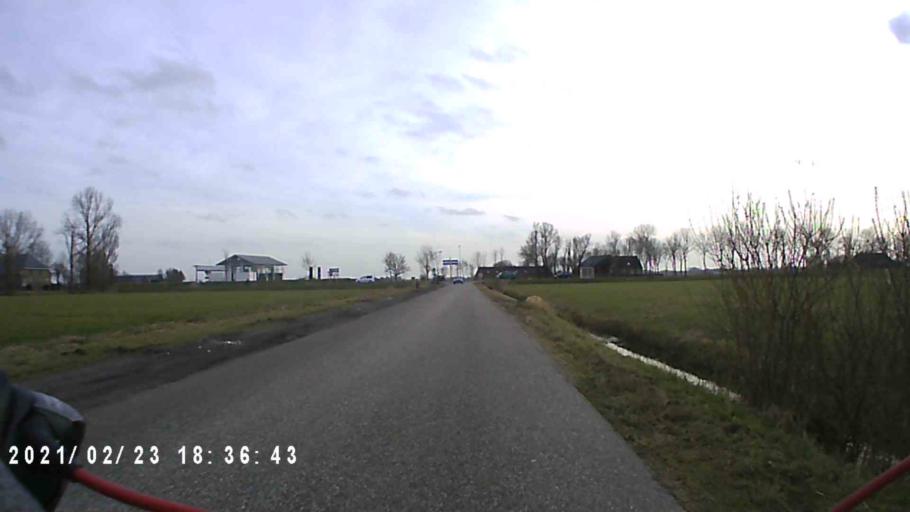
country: NL
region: Groningen
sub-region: Gemeente Bedum
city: Bedum
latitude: 53.3384
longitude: 6.6046
